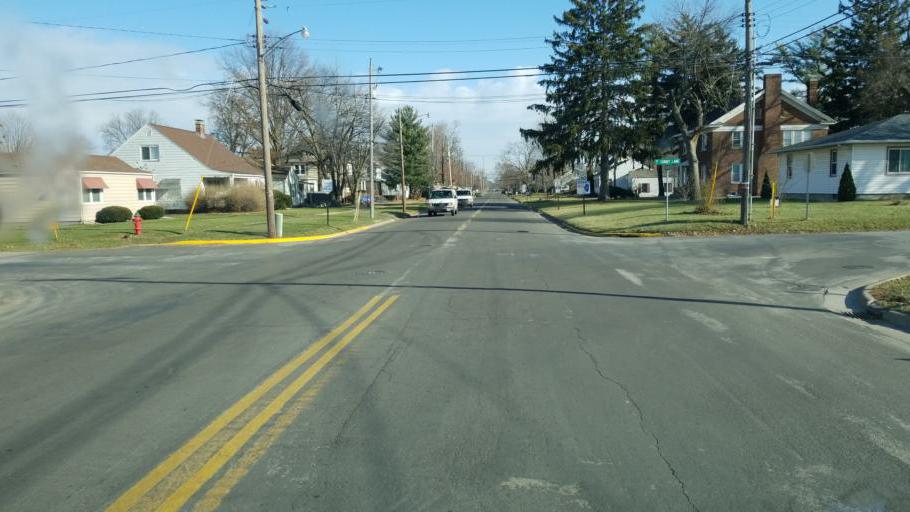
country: US
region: Illinois
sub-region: Warren County
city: Monmouth
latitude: 40.9123
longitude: -90.6605
